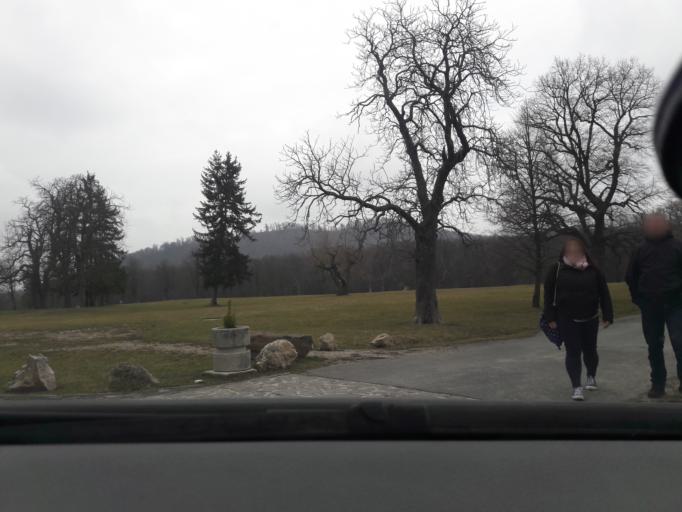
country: SK
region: Bratislavsky
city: Modra
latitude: 48.3940
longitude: 17.3348
